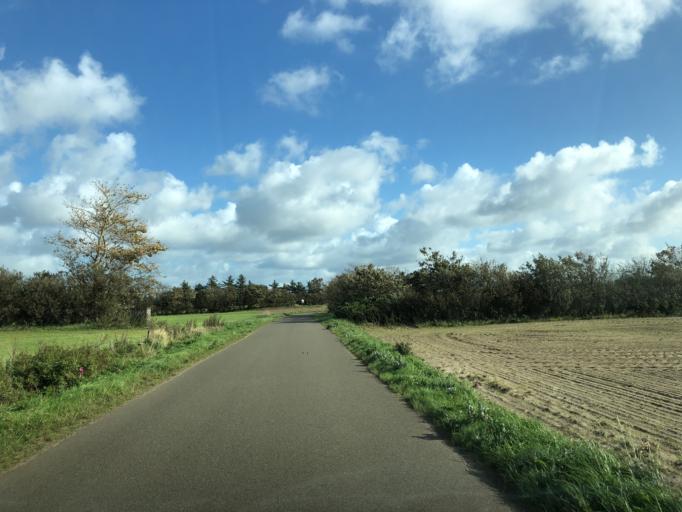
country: DK
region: Central Jutland
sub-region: Holstebro Kommune
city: Ulfborg
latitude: 56.2904
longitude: 8.3259
